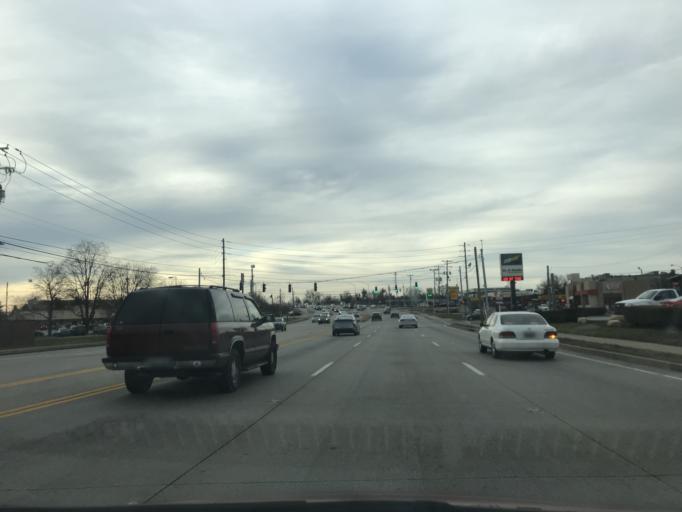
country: US
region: Kentucky
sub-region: Jefferson County
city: West Buechel
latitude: 38.1996
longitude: -85.6841
